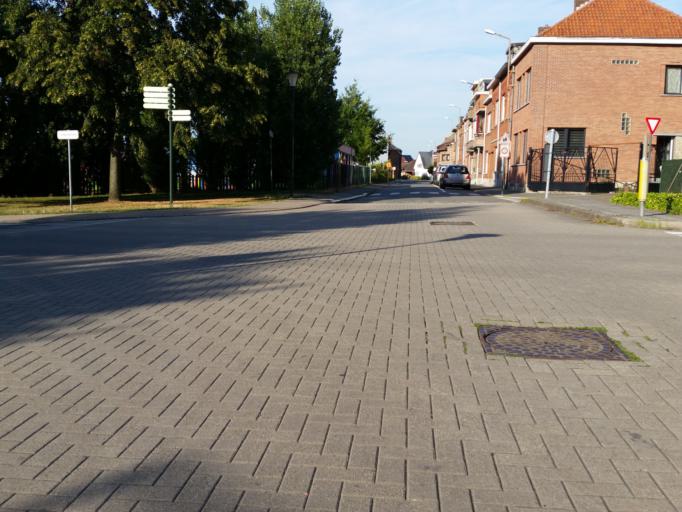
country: BE
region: Flanders
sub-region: Provincie Vlaams-Brabant
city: Machelen
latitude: 50.9092
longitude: 4.4368
